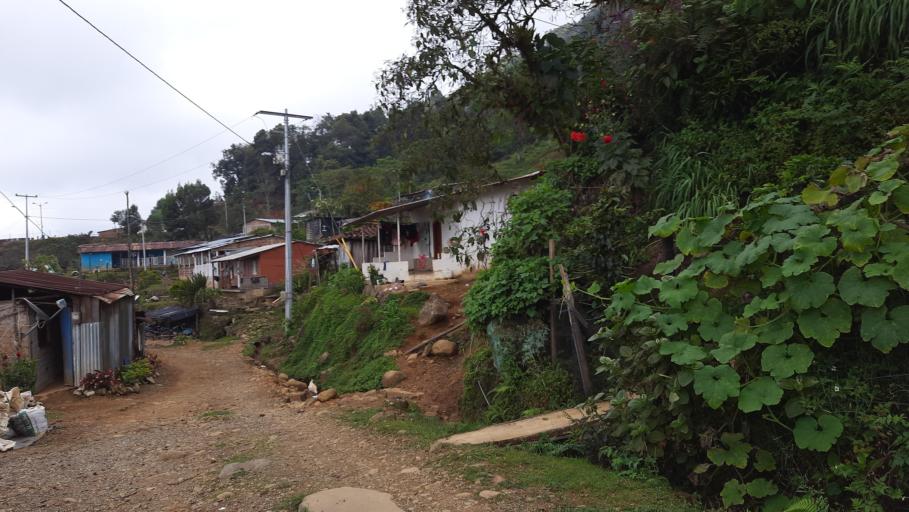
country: CO
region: Cauca
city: Buenos Aires
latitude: 3.1795
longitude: -76.7237
